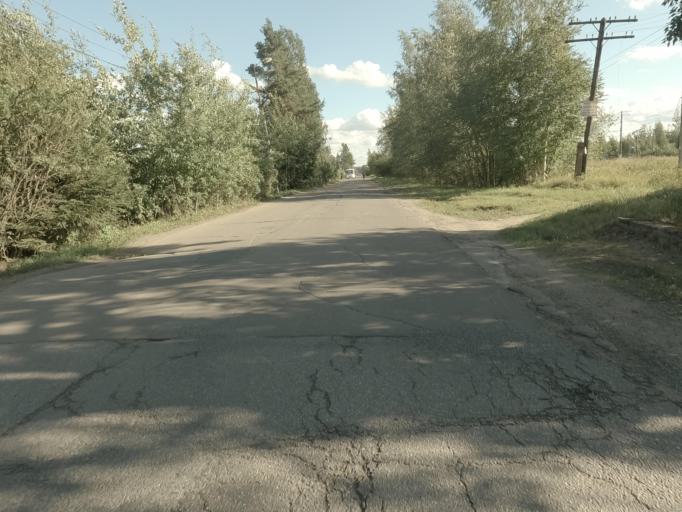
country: RU
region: Leningrad
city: Imeni Morozova
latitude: 59.9644
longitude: 31.0294
